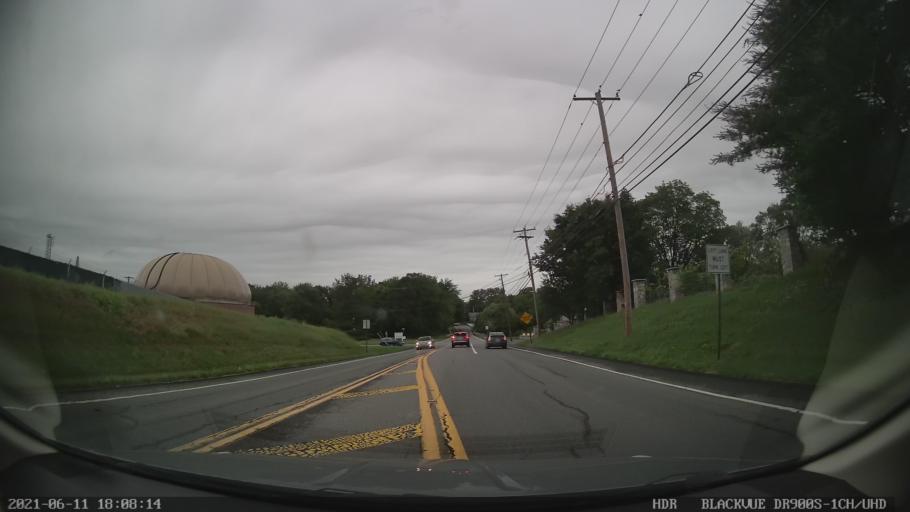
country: US
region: Pennsylvania
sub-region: Berks County
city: Whitfield
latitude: 40.3471
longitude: -76.0052
